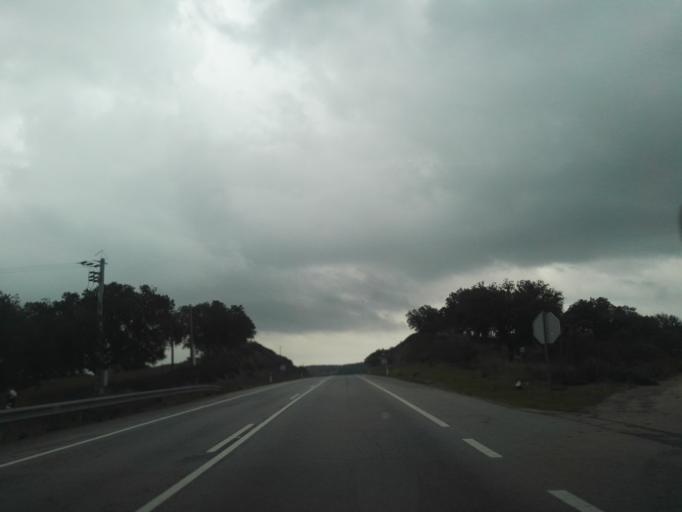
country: PT
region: Portalegre
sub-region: Portalegre
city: Alegrete
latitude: 39.1884
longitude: -7.3519
